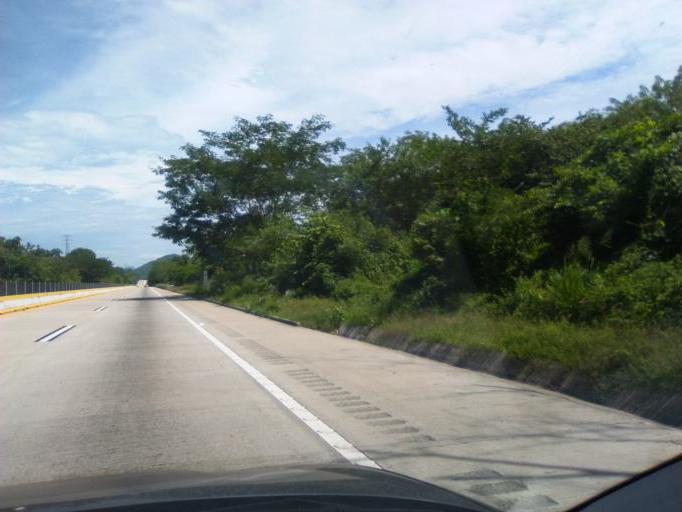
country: MX
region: Guerrero
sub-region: Acapulco de Juarez
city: Kilometro 30
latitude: 17.0002
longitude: -99.6868
